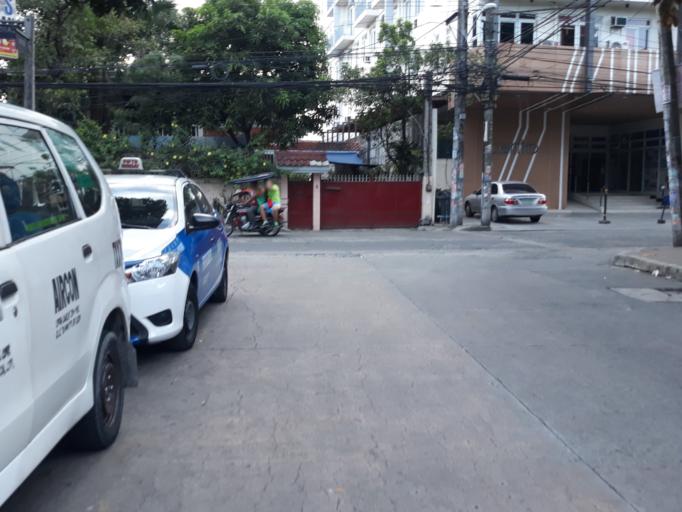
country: PH
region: Metro Manila
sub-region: San Juan
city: San Juan
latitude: 14.6174
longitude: 121.0457
